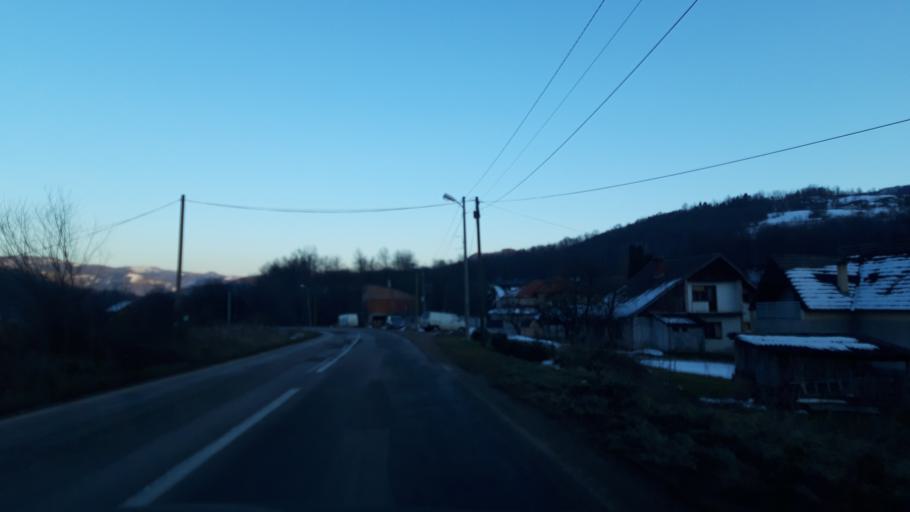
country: BA
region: Republika Srpska
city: Milici
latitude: 44.1640
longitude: 19.0466
